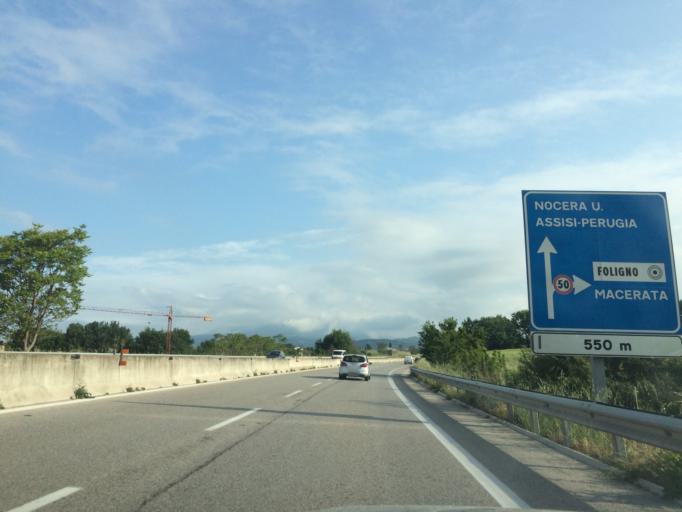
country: IT
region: Umbria
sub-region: Provincia di Perugia
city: Foligno
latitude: 42.9389
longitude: 12.7227
